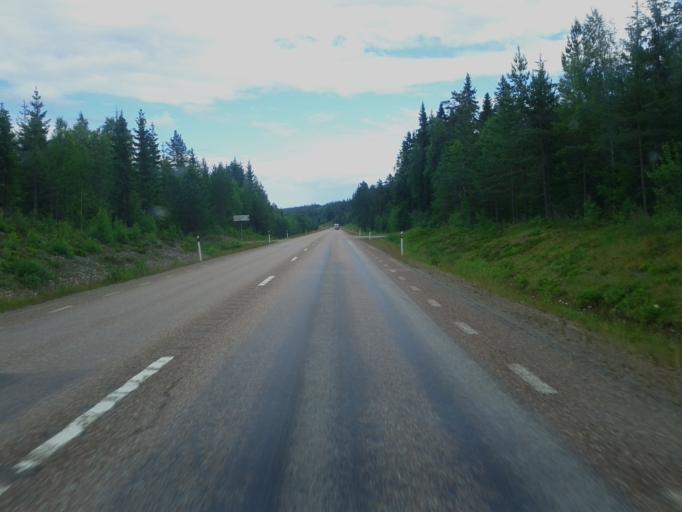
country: SE
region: Dalarna
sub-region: Faluns Kommun
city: Bjursas
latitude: 60.7547
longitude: 15.3424
